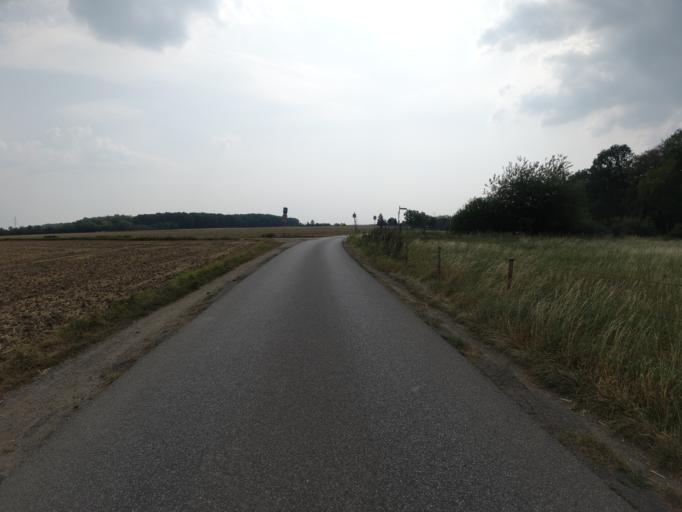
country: DE
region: North Rhine-Westphalia
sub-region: Regierungsbezirk Dusseldorf
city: Moers
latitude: 51.4166
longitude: 6.6416
